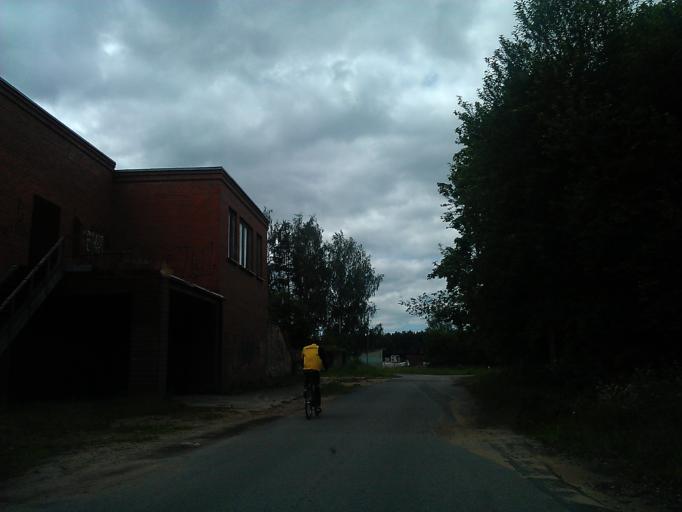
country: LV
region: Riga
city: Bergi
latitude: 57.0000
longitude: 24.2898
